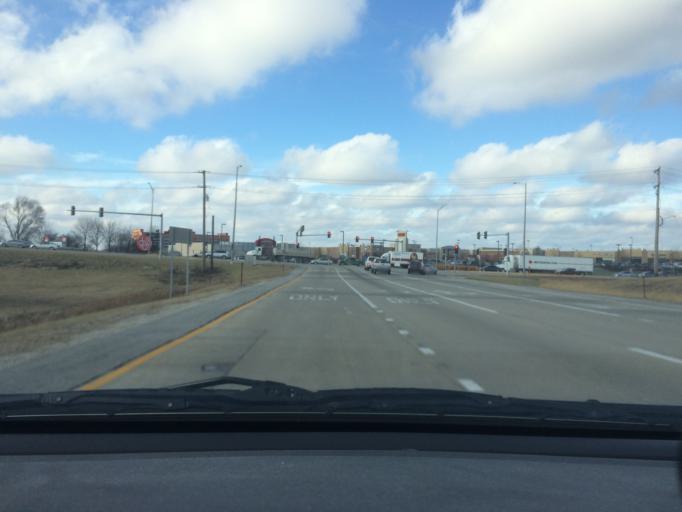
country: US
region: Illinois
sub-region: Cook County
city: Streamwood
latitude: 42.0687
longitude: -88.1902
